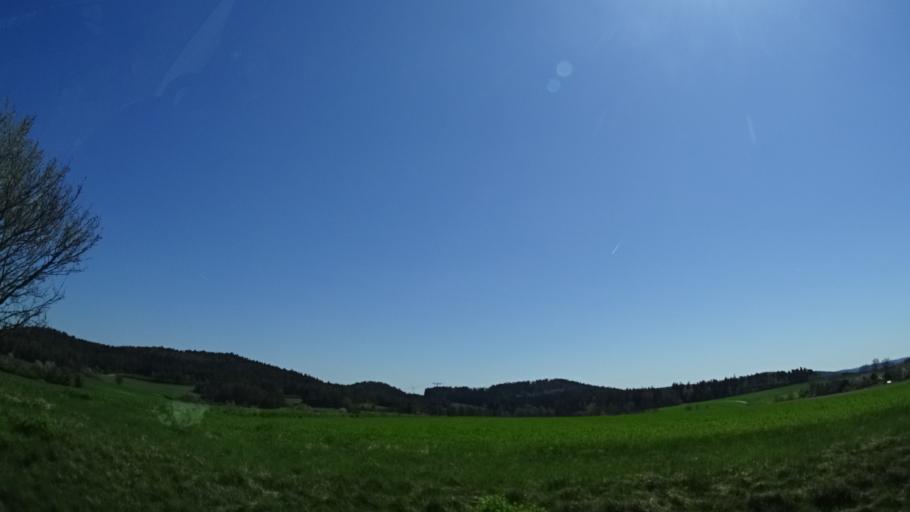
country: DE
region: Bavaria
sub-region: Upper Palatinate
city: Kastl
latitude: 49.3834
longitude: 11.7024
